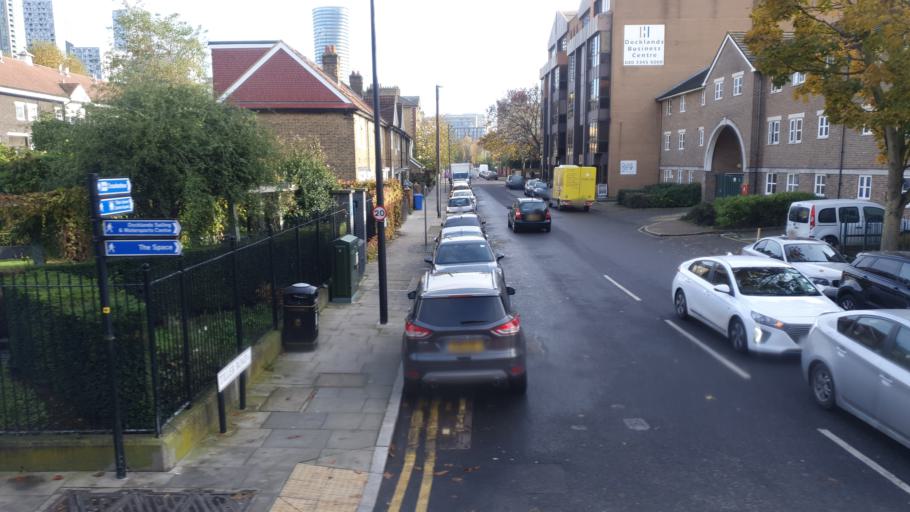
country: GB
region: England
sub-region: Greater London
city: Poplar
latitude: 51.4963
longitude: -0.0257
